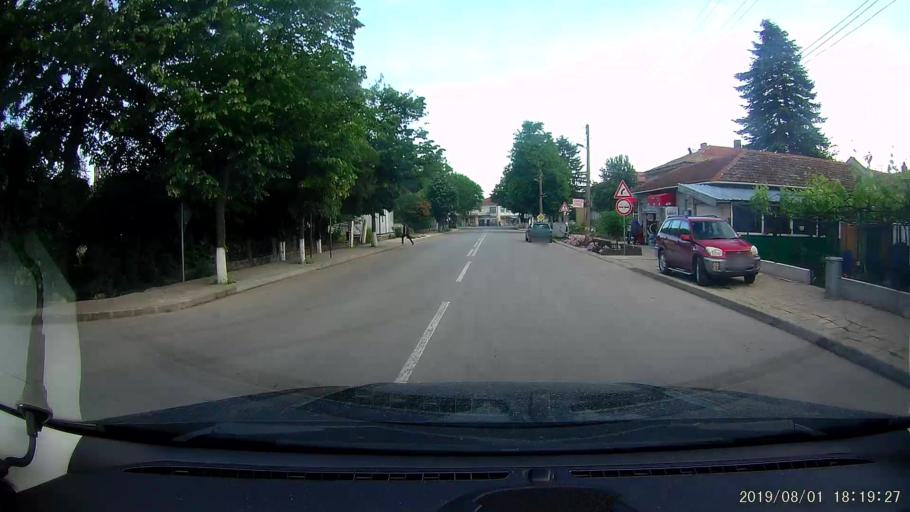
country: BG
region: Shumen
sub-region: Obshtina Kaolinovo
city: Kaolinovo
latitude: 43.6833
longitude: 27.0908
